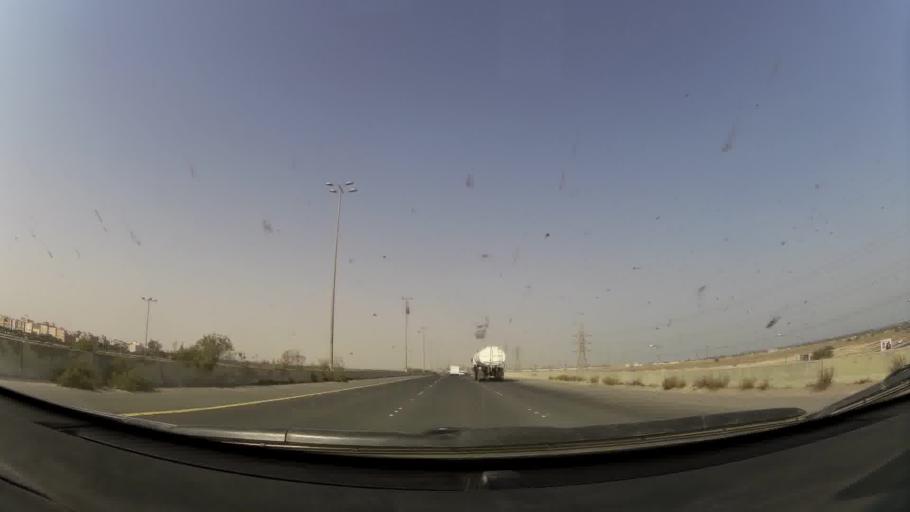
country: KW
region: Al Ahmadi
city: Al Fahahil
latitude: 28.9653
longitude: 48.1651
